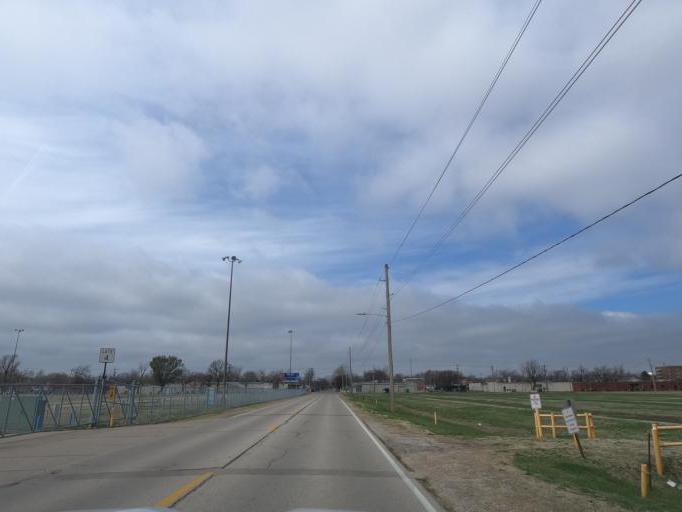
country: US
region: Kansas
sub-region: Reno County
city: Hutchinson
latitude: 38.0811
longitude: -97.9291
